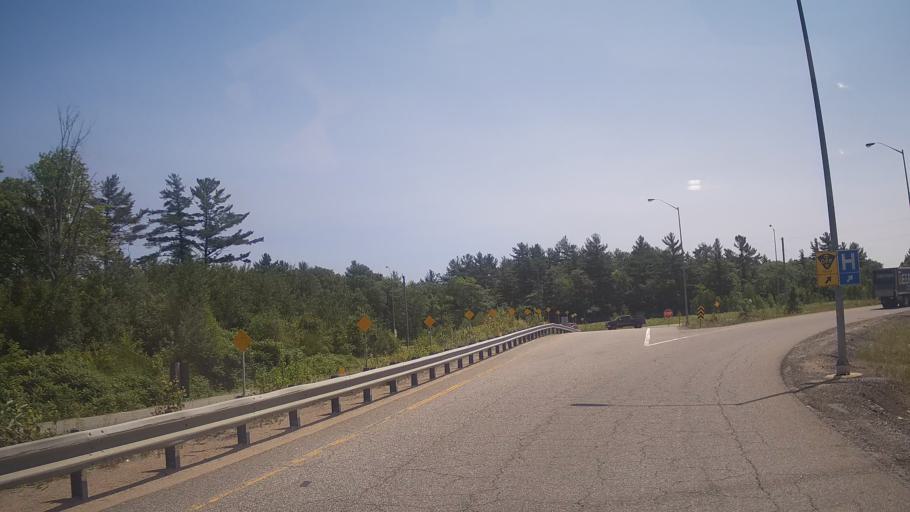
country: CA
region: Ontario
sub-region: Parry Sound District
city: Parry Sound
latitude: 45.3493
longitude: -80.0013
